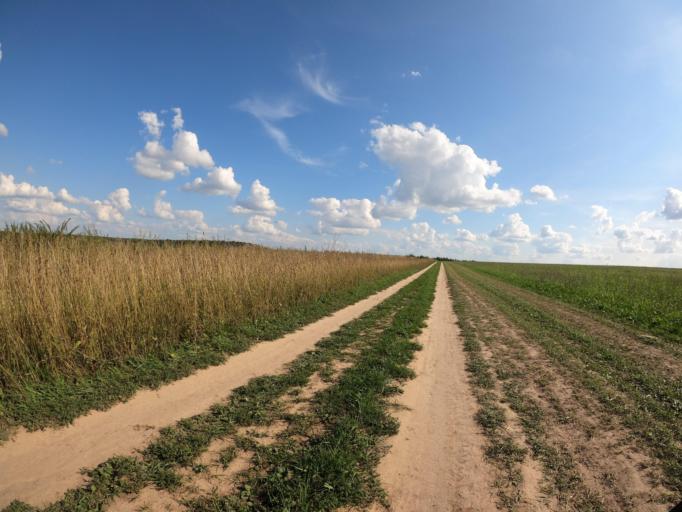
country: RU
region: Moskovskaya
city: Troitskoye
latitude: 55.2231
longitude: 38.4860
